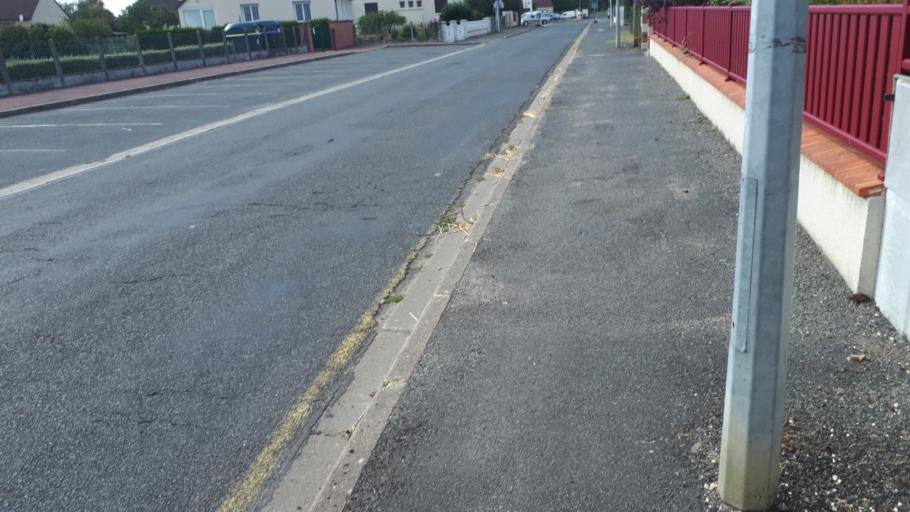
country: FR
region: Centre
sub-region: Departement du Loiret
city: Poilly-lez-Gien
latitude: 47.6771
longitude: 2.5958
